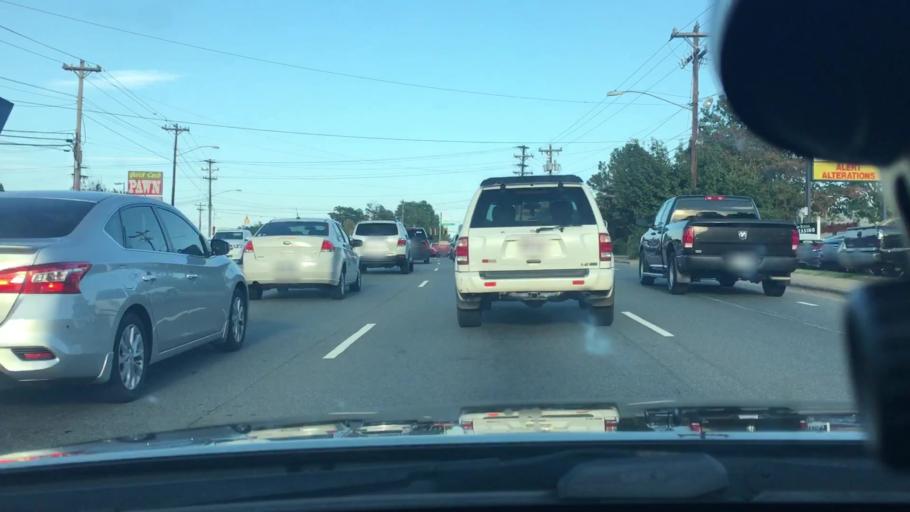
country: US
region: North Carolina
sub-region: Mecklenburg County
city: Mint Hill
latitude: 35.2023
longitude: -80.7277
